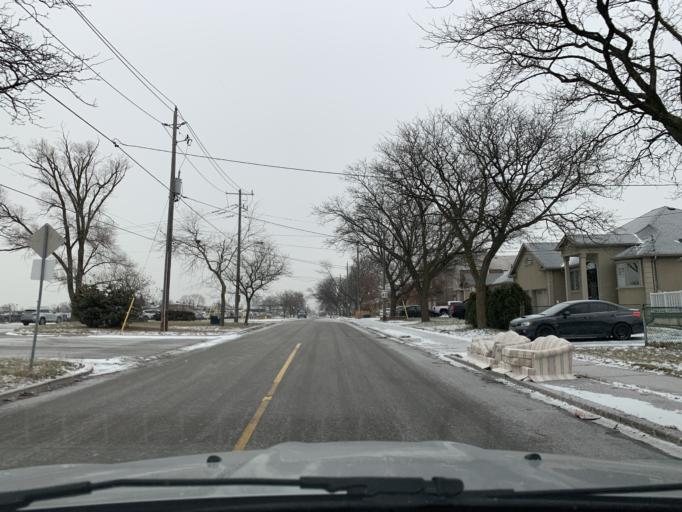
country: CA
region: Ontario
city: Toronto
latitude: 43.7332
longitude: -79.4724
